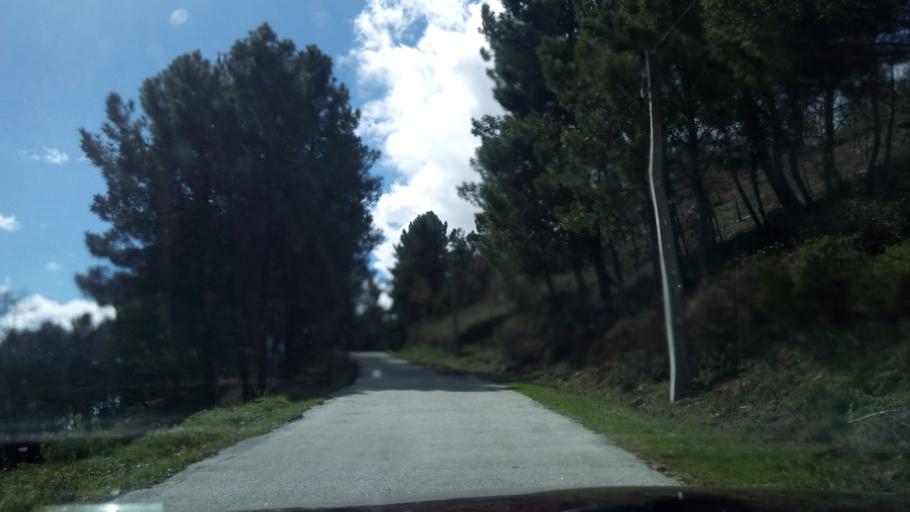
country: PT
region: Guarda
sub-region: Fornos de Algodres
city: Fornos de Algodres
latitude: 40.6615
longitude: -7.5000
